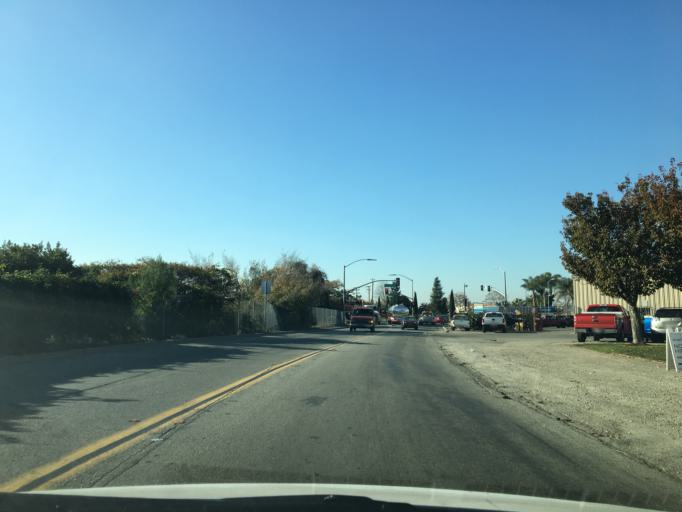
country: US
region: California
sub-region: Santa Clara County
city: San Jose
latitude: 37.3626
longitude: -121.8844
